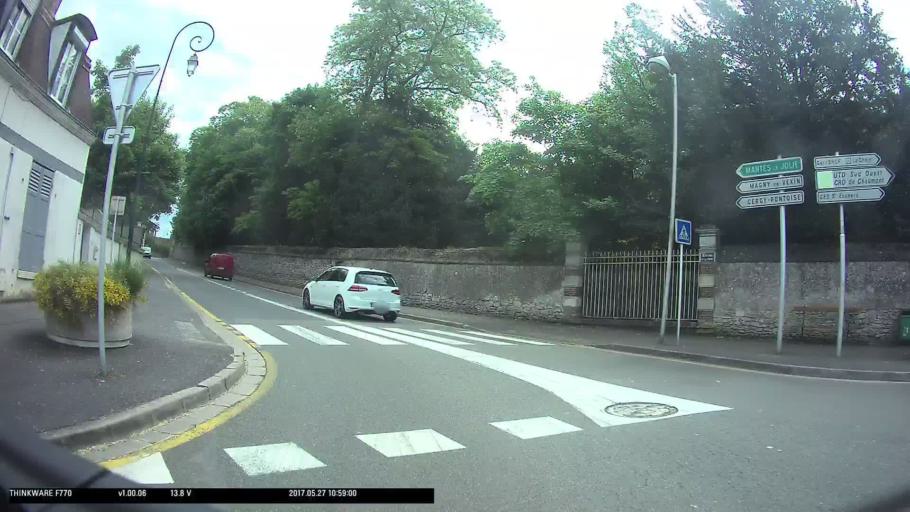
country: FR
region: Picardie
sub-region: Departement de l'Oise
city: Chaumont-en-Vexin
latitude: 49.2624
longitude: 1.8765
